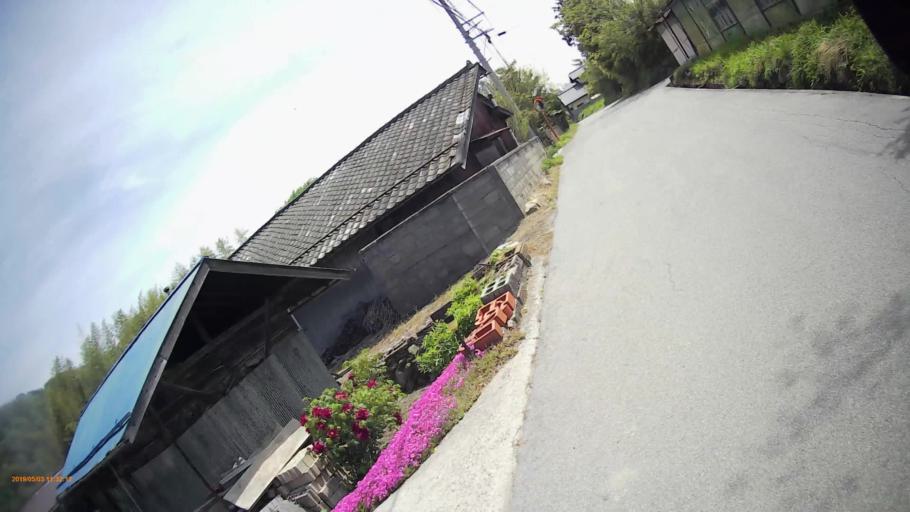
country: JP
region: Nagano
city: Chino
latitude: 35.8472
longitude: 138.2983
